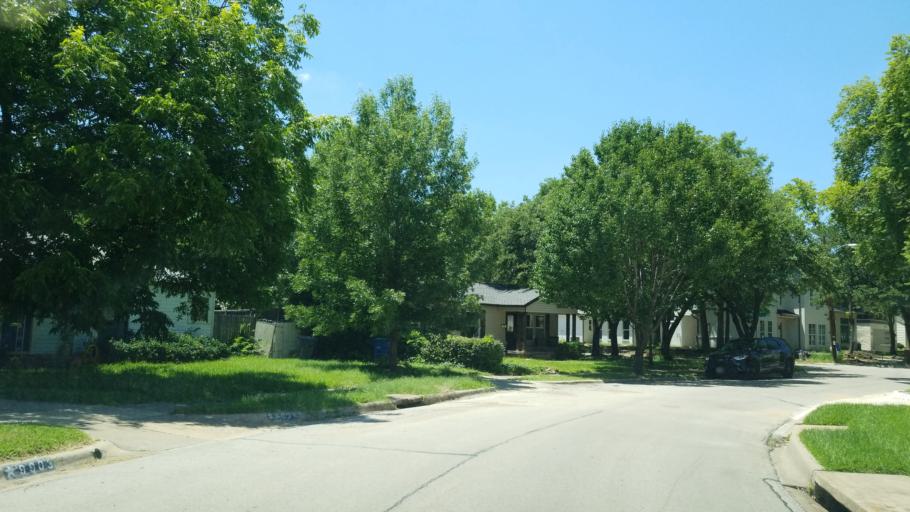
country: US
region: Texas
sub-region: Dallas County
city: University Park
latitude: 32.8772
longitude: -96.8512
